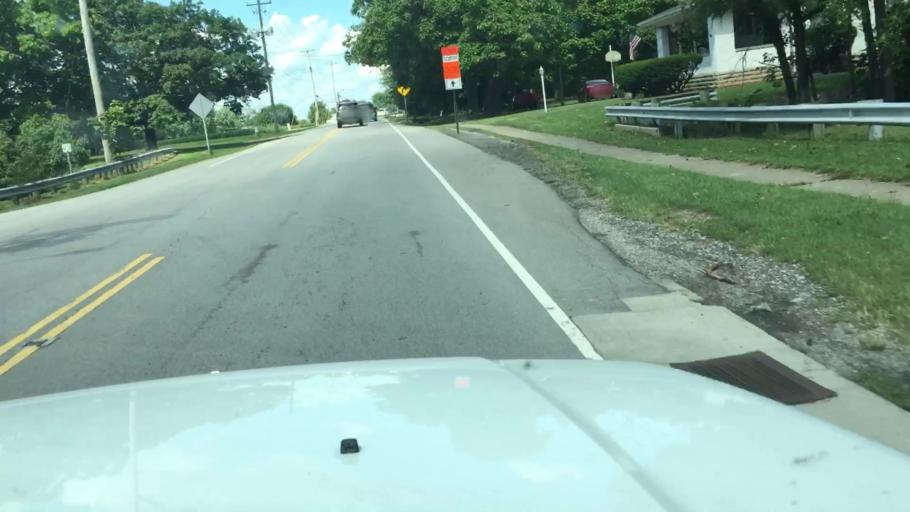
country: US
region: Ohio
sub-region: Madison County
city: Mount Sterling
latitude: 39.7252
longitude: -83.2699
